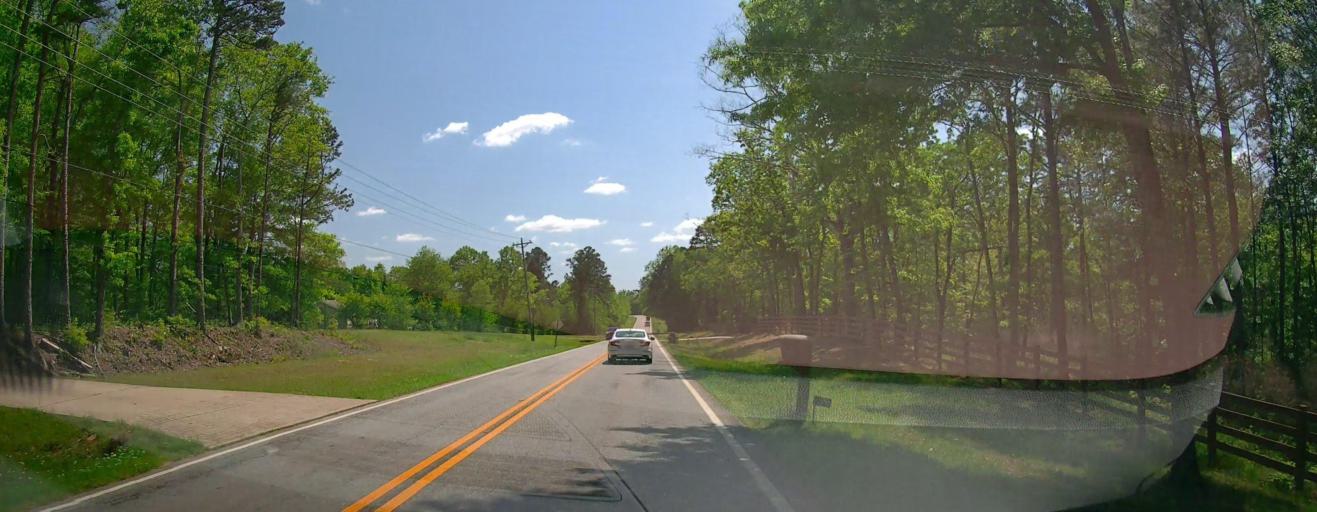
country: US
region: Georgia
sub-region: Putnam County
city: Eatonton
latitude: 33.2869
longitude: -83.3020
